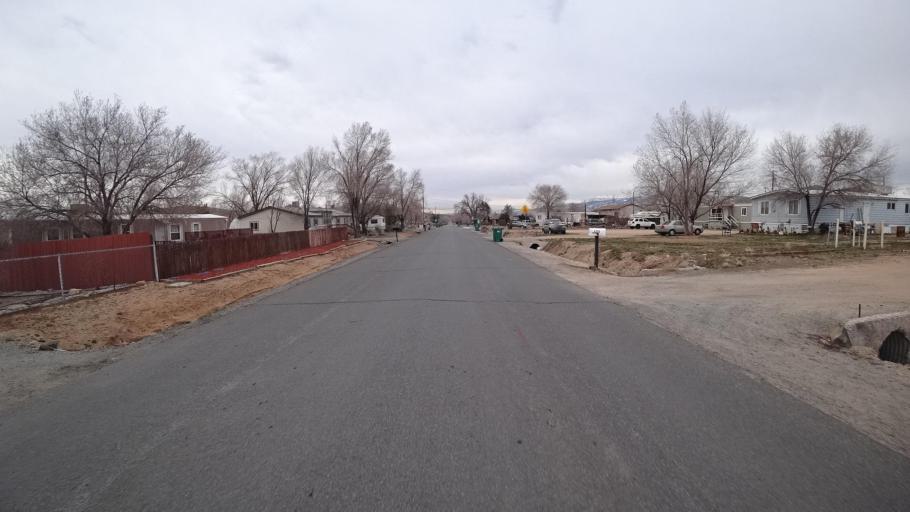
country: US
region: Nevada
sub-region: Washoe County
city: Sun Valley
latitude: 39.6011
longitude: -119.7711
